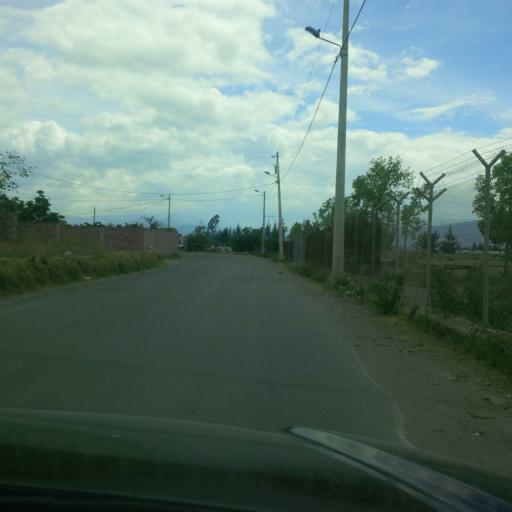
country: EC
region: Chimborazo
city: Riobamba
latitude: -1.6467
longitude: -78.6518
